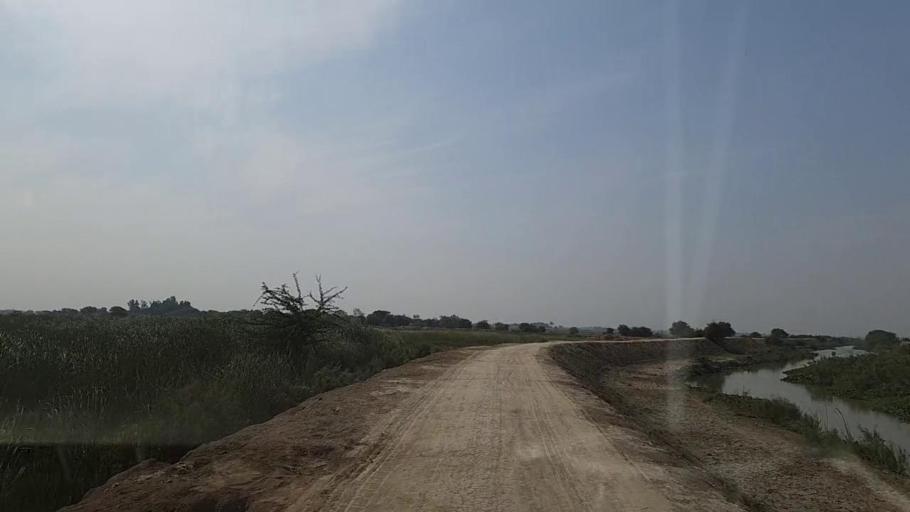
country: PK
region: Sindh
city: Mirpur Batoro
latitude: 24.6560
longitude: 68.2462
